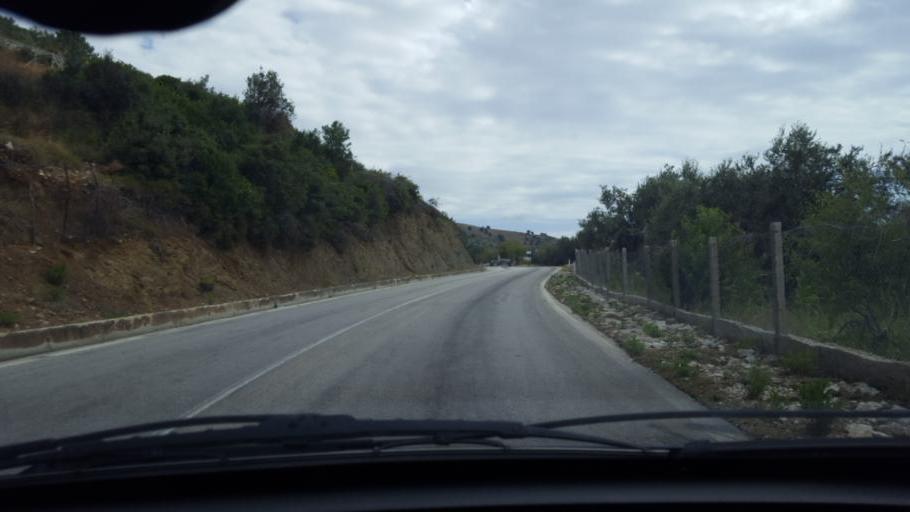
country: AL
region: Vlore
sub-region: Rrethi i Sarandes
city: Lukove
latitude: 40.0572
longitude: 19.8638
